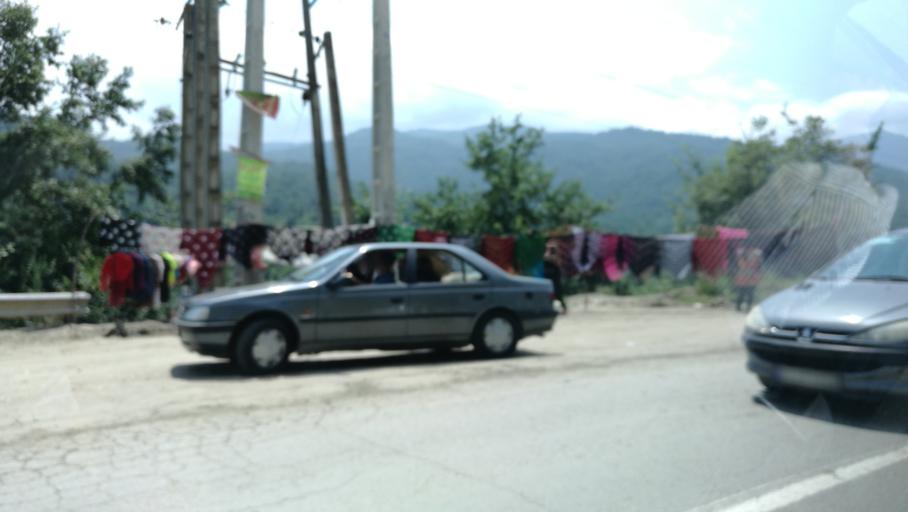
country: IR
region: Mazandaran
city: Ramsar
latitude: 36.9021
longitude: 50.5969
